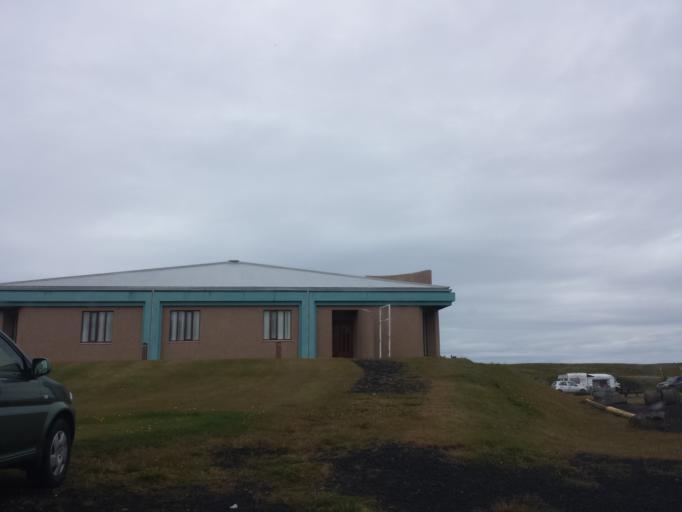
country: IS
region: Southern Peninsula
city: Sandgerdi
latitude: 64.0390
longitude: -22.6990
